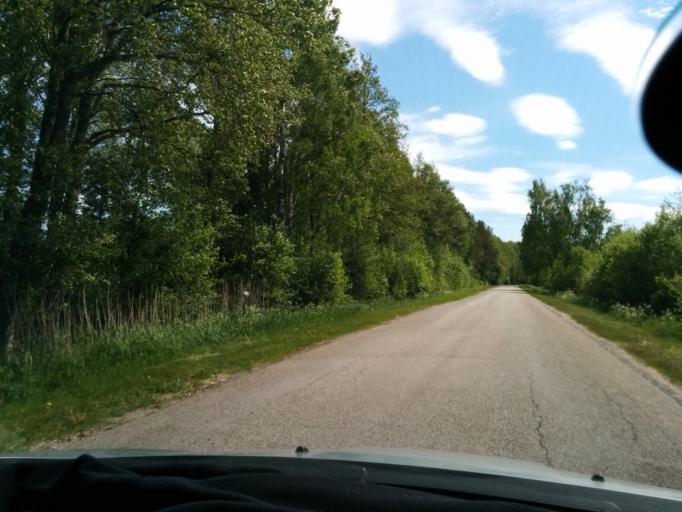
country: EE
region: Harju
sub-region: Loksa linn
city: Loksa
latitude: 59.5819
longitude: 25.9131
